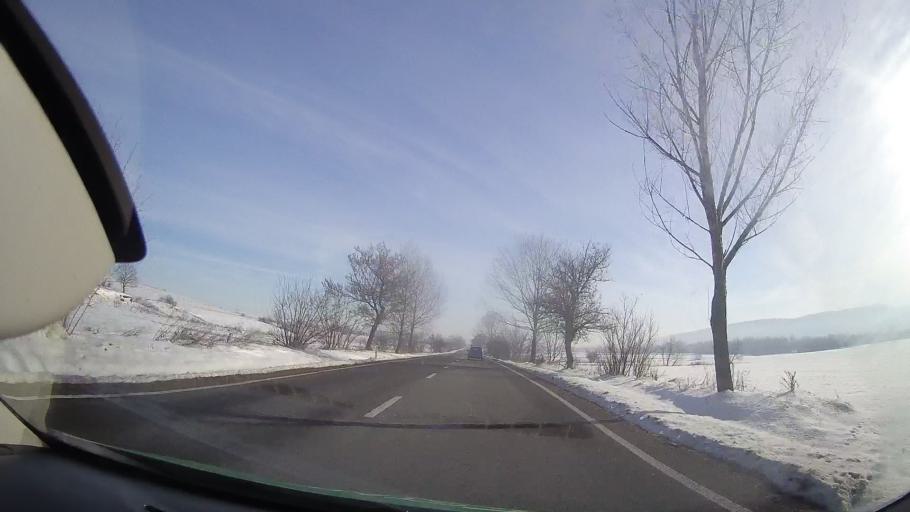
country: RO
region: Neamt
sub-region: Comuna Negresti
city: Negresti
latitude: 47.0673
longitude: 26.3711
